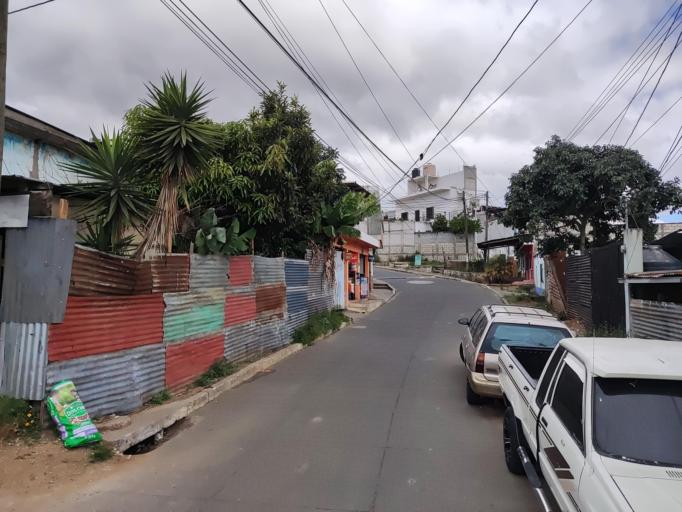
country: GT
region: Guatemala
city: Mixco
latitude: 14.5857
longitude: -90.6046
